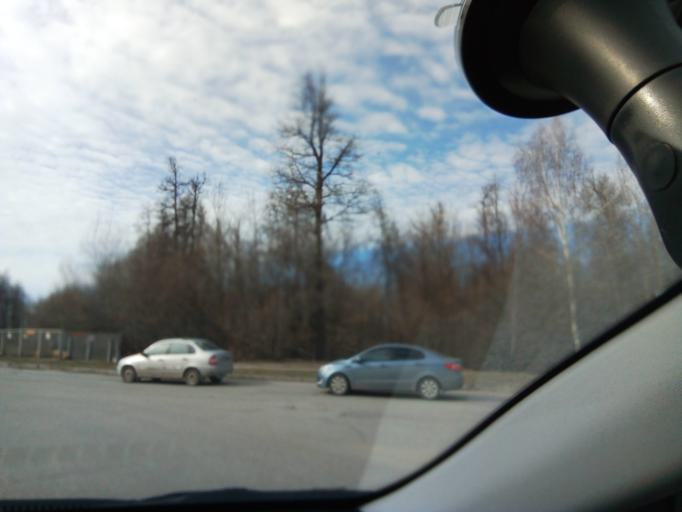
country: RU
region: Chuvashia
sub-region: Cheboksarskiy Rayon
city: Cheboksary
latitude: 56.0972
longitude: 47.2592
